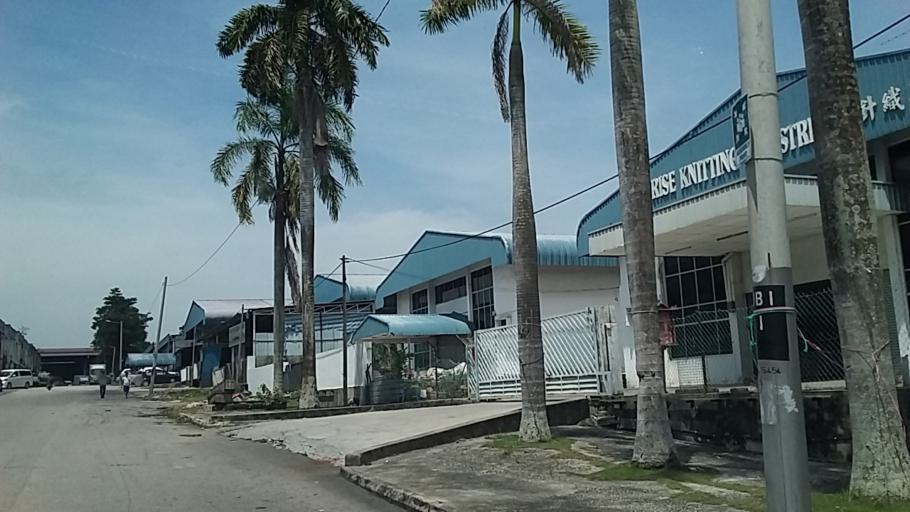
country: MY
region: Johor
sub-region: Daerah Batu Pahat
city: Batu Pahat
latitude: 1.7871
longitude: 102.9680
